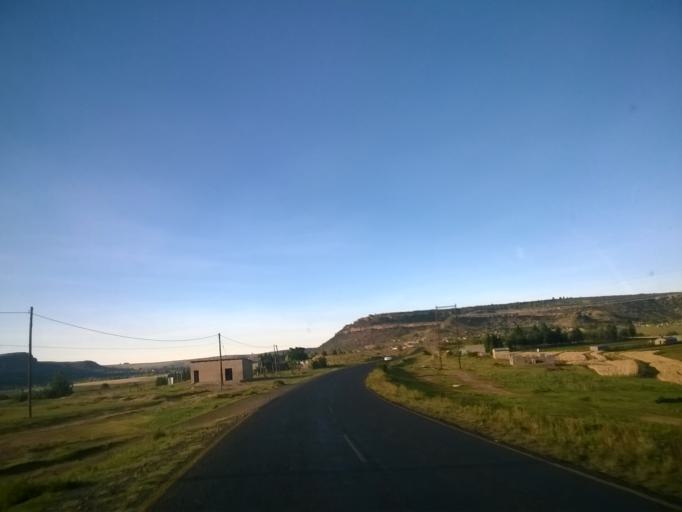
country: LS
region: Berea
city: Teyateyaneng
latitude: -29.2185
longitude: 27.6165
